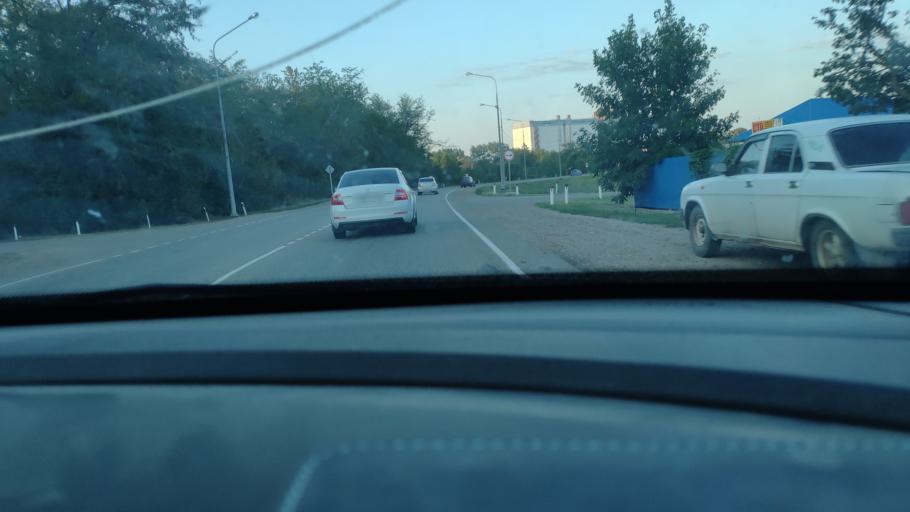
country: RU
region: Krasnodarskiy
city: Novominskaya
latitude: 46.3229
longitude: 38.9346
